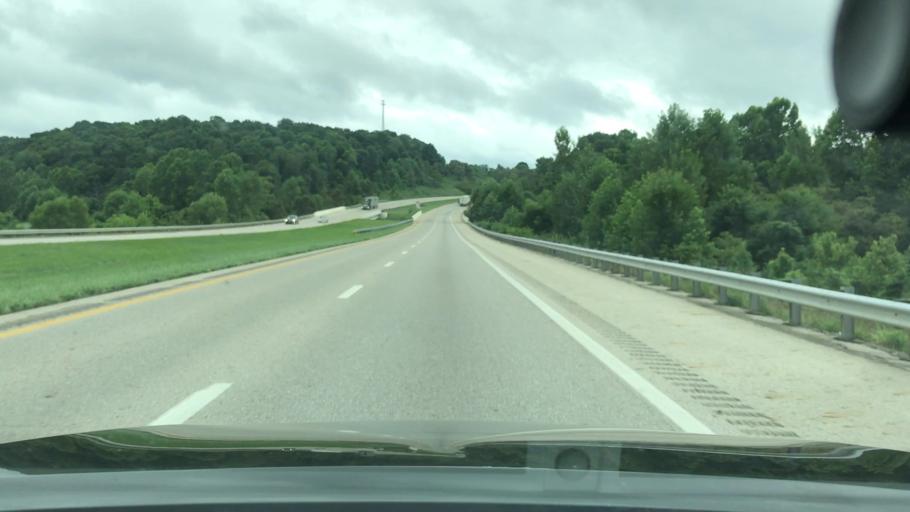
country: US
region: Ohio
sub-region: Ross County
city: Chillicothe
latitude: 39.2567
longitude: -82.8567
